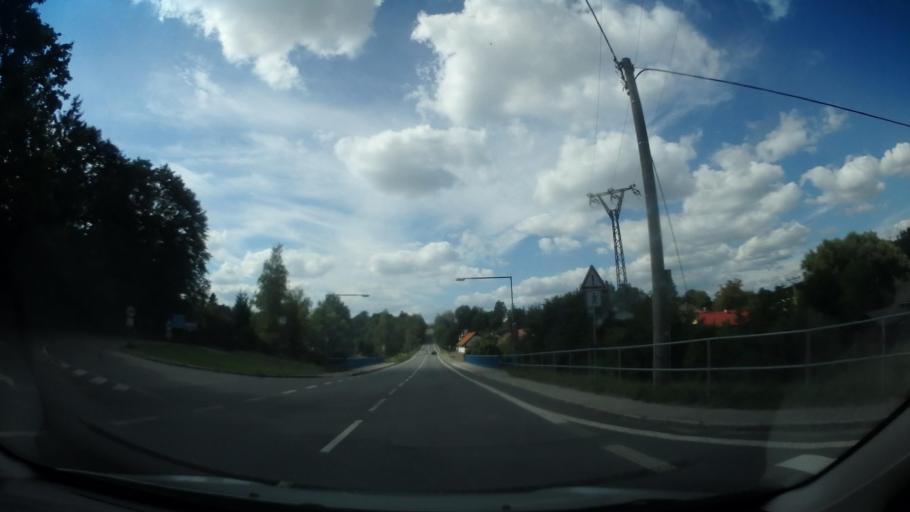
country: CZ
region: Vysocina
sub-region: Okres Zd'ar nad Sazavou
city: Nove Veseli
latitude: 49.5602
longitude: 15.8628
